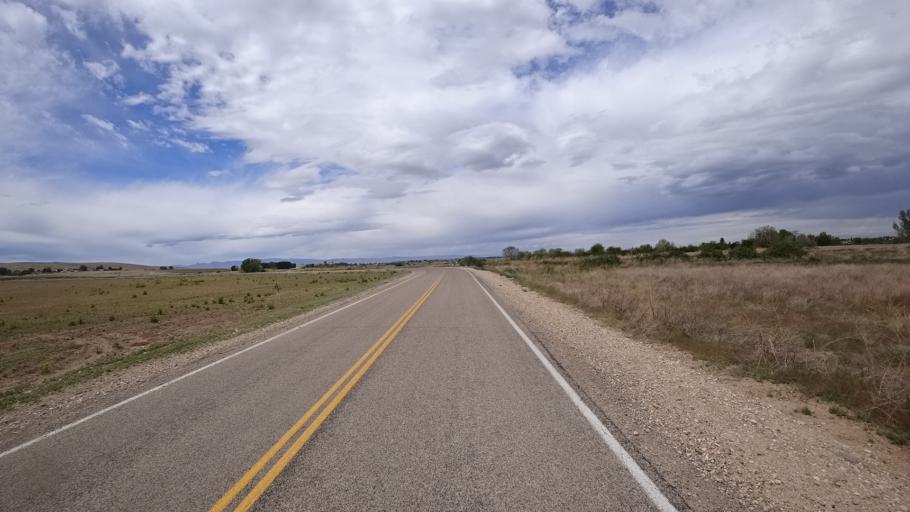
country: US
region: Idaho
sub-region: Ada County
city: Kuna
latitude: 43.4700
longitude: -116.4410
